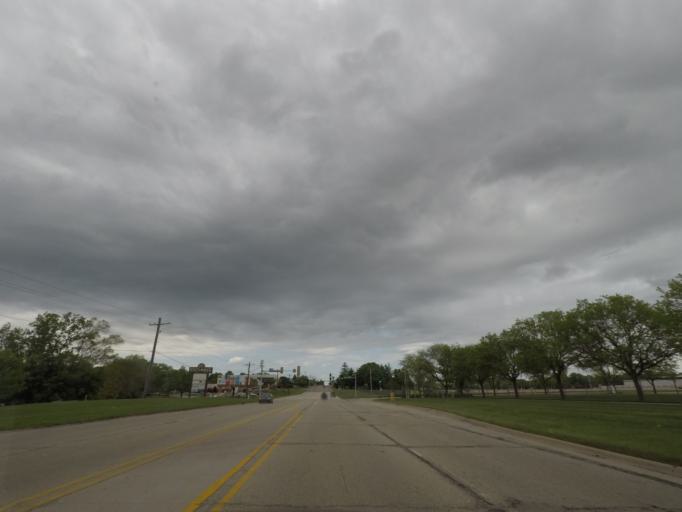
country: US
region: Illinois
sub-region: Winnebago County
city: Rockford
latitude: 42.2346
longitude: -89.0290
